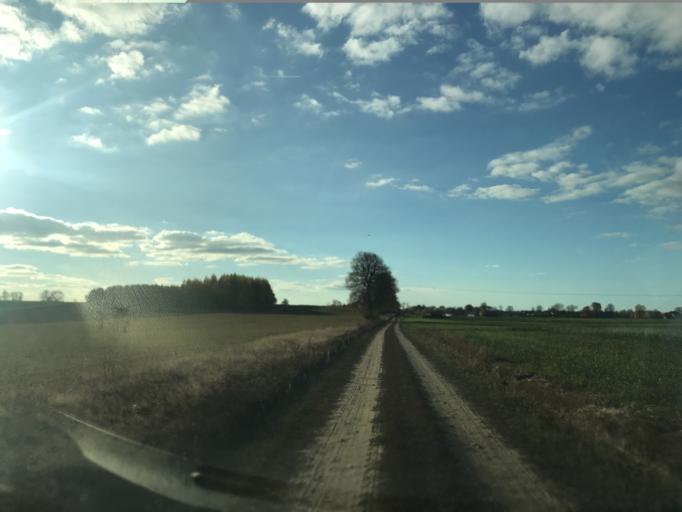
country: PL
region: Warmian-Masurian Voivodeship
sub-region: Powiat dzialdowski
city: Lidzbark
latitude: 53.3630
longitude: 19.8080
